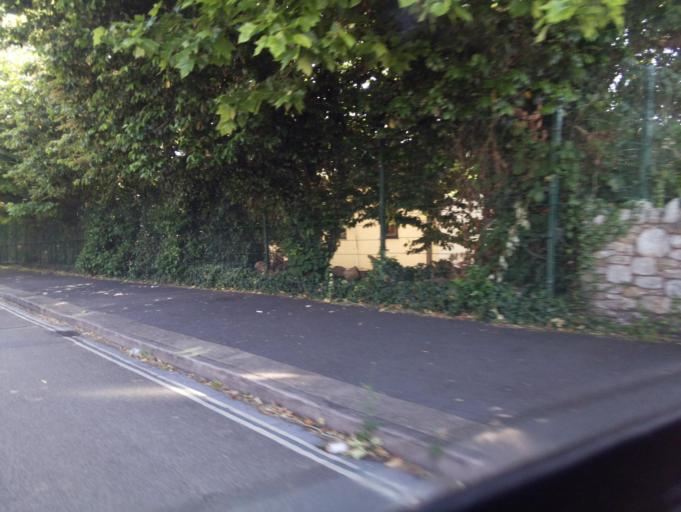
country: GB
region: England
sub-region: Borough of Torbay
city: Torquay
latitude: 50.4676
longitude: -3.5436
